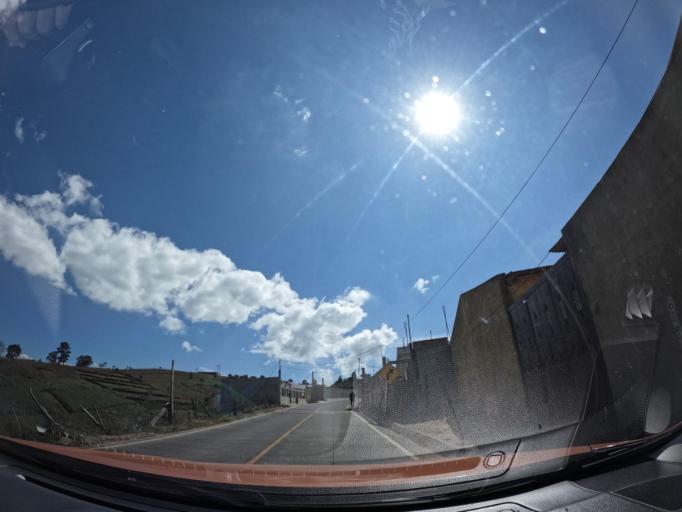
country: GT
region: Chimaltenango
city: Patzun
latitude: 14.6577
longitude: -91.0542
